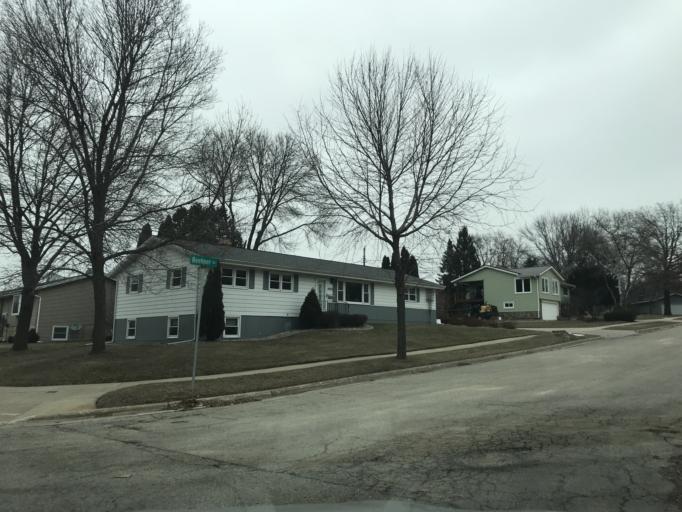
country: US
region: Wisconsin
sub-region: Dane County
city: Monona
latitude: 43.0971
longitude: -89.2984
